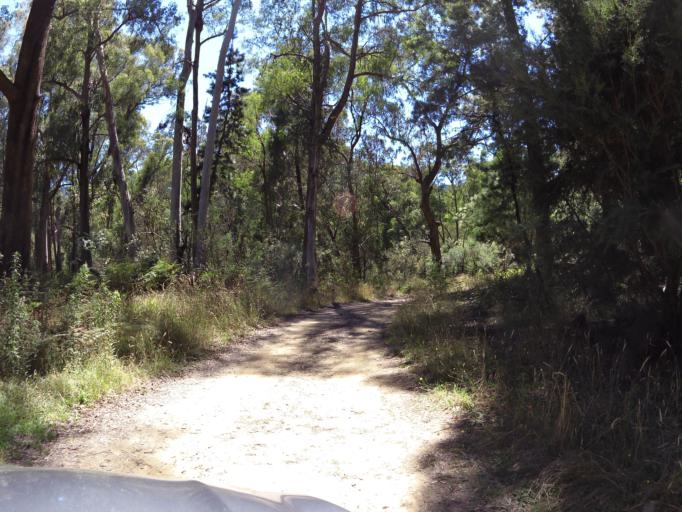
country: AU
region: Victoria
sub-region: Alpine
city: Mount Beauty
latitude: -36.7259
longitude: 146.9862
